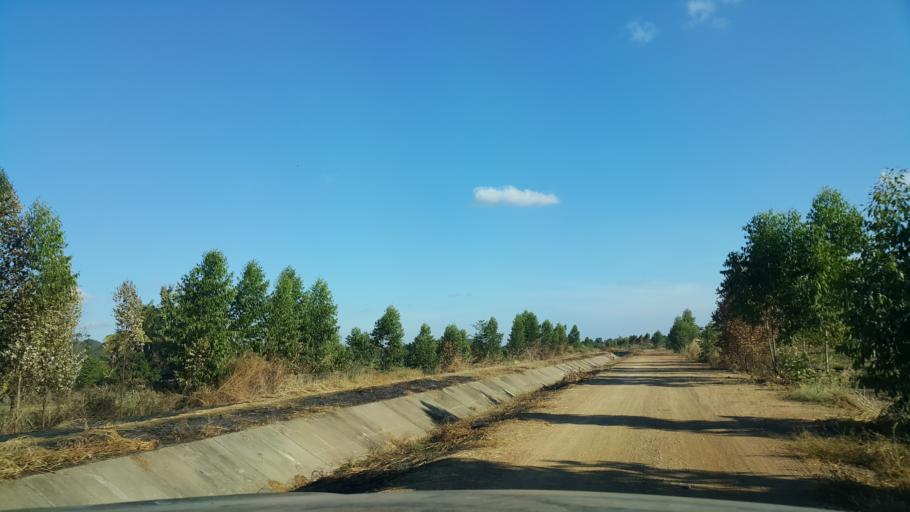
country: TH
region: Sukhothai
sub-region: Amphoe Si Satchanalai
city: Si Satchanalai
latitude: 17.4818
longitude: 99.6513
